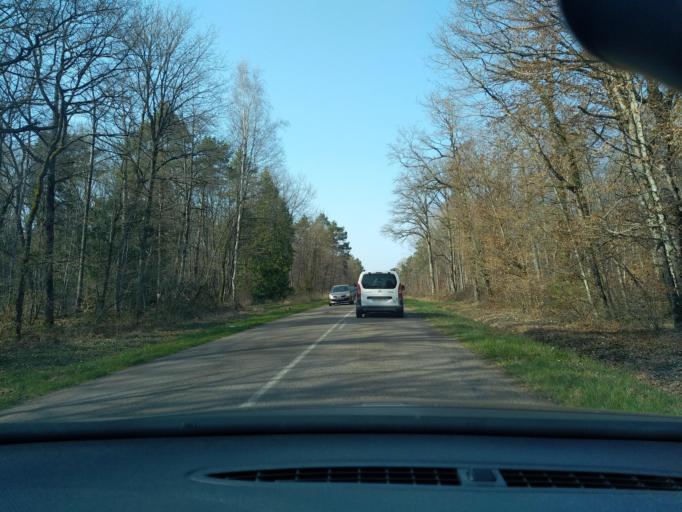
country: FR
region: Franche-Comte
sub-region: Departement du Jura
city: Dole
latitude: 47.0630
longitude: 5.5091
